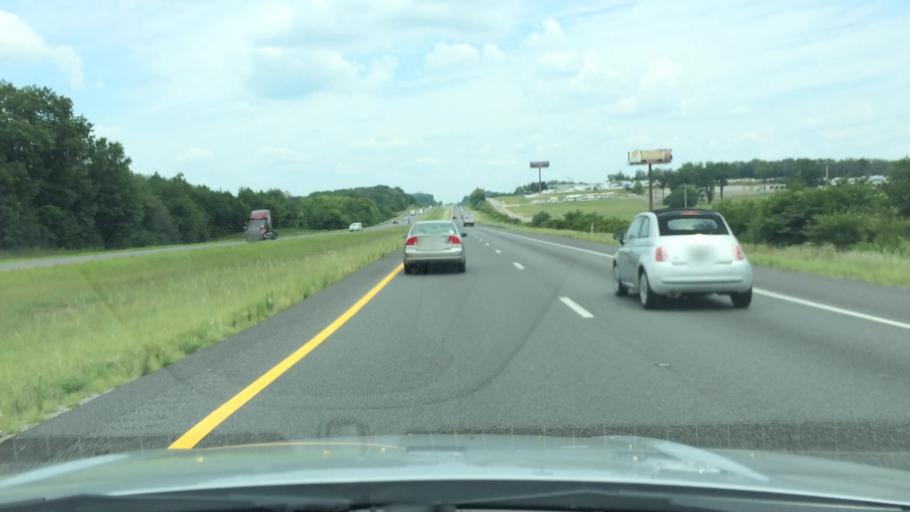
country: US
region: Tennessee
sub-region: Maury County
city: Spring Hill
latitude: 35.6938
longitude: -86.8845
